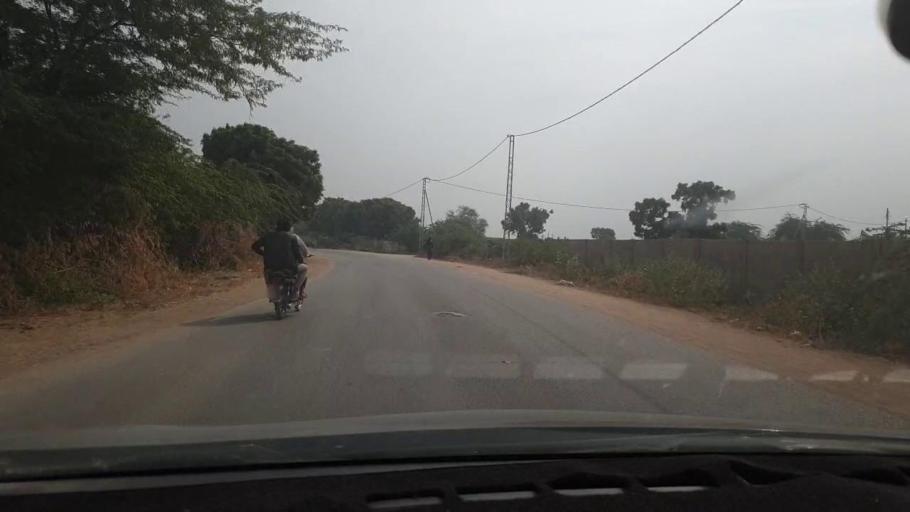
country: PK
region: Sindh
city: Malir Cantonment
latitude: 24.9145
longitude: 67.2615
